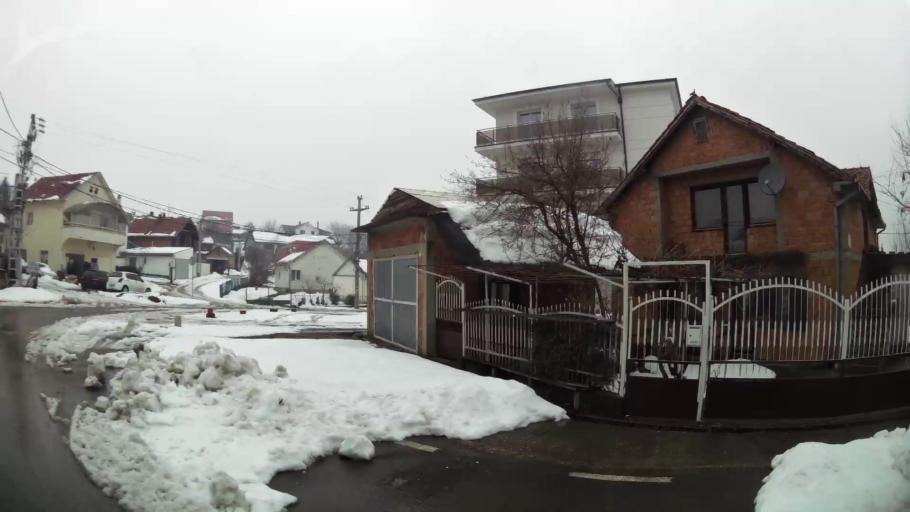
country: RS
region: Central Serbia
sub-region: Belgrade
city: Zvezdara
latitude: 44.7537
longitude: 20.5227
